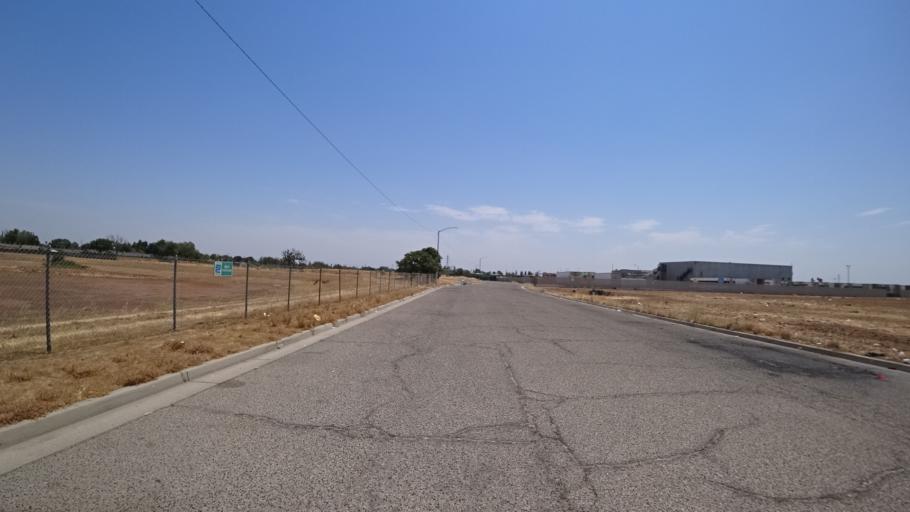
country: US
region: California
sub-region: Fresno County
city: West Park
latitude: 36.7178
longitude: -119.8260
